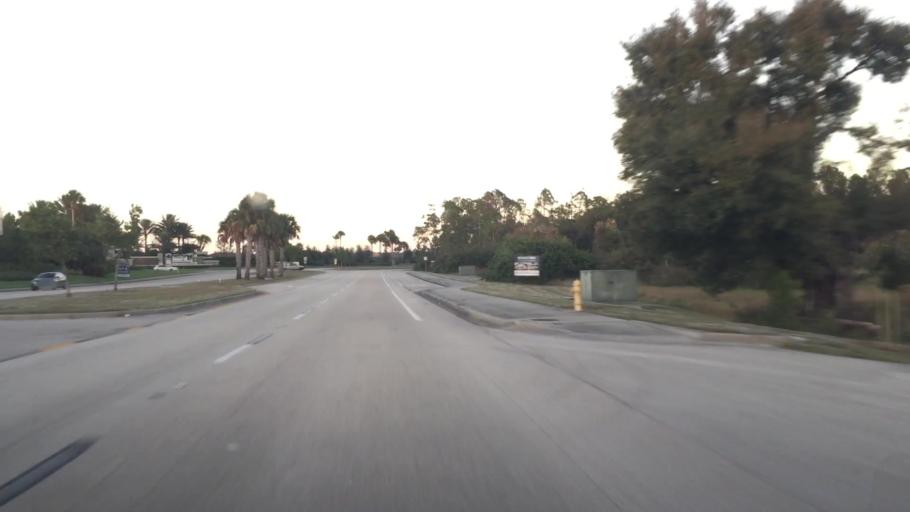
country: US
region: Florida
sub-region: Lee County
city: Gateway
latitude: 26.5703
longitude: -81.7817
